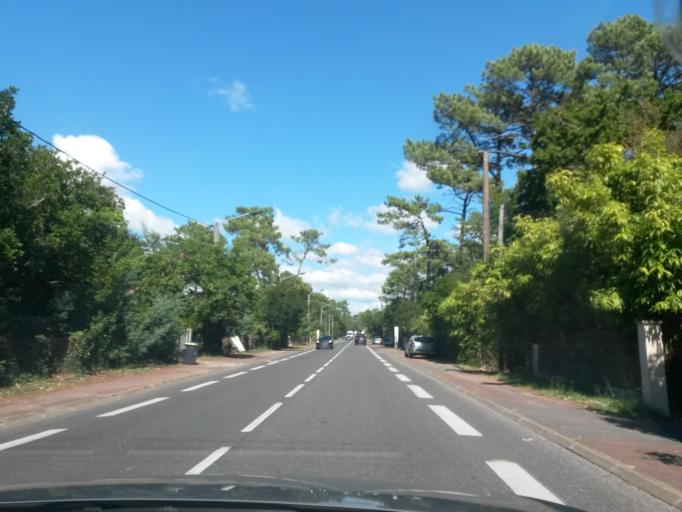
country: FR
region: Aquitaine
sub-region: Departement de la Gironde
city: Arcachon
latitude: 44.7121
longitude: -1.2186
